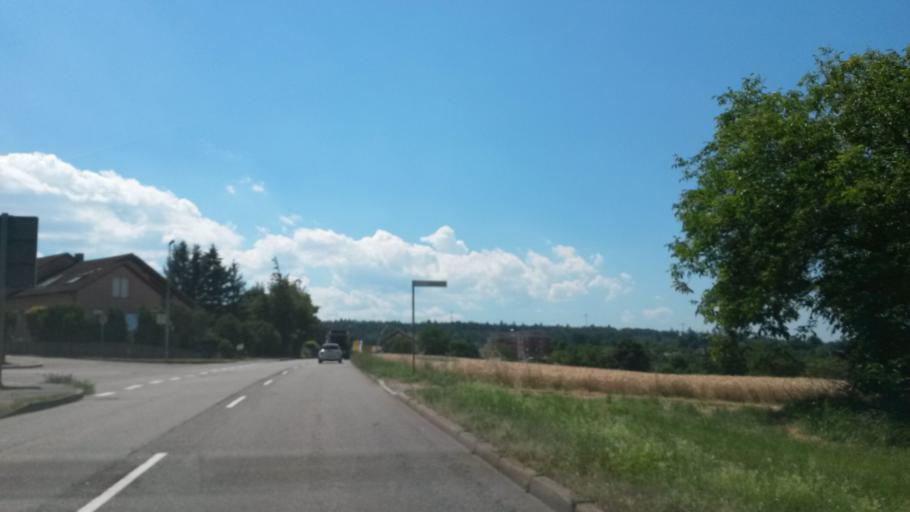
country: DE
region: Baden-Wuerttemberg
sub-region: Karlsruhe Region
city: Birkenfeld
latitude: 48.8739
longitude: 8.6290
